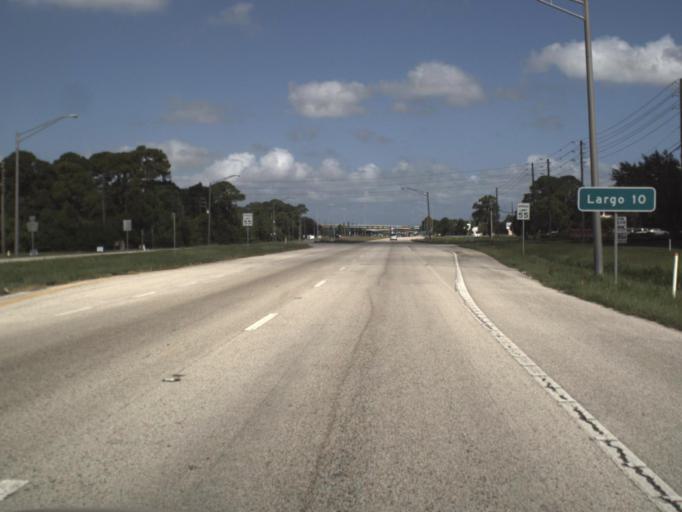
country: US
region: Florida
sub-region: Pinellas County
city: Gandy
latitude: 27.8714
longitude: -82.6488
